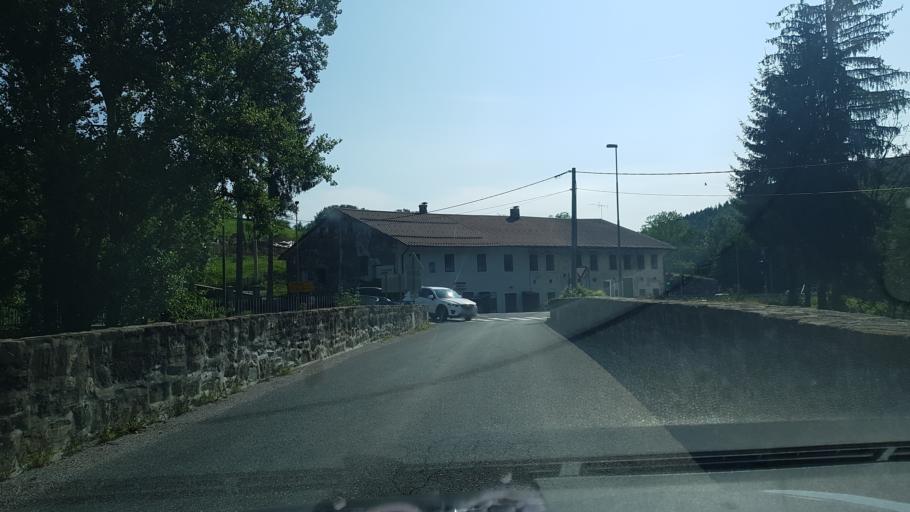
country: SI
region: Pivka
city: Pivka
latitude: 45.6084
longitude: 14.1791
